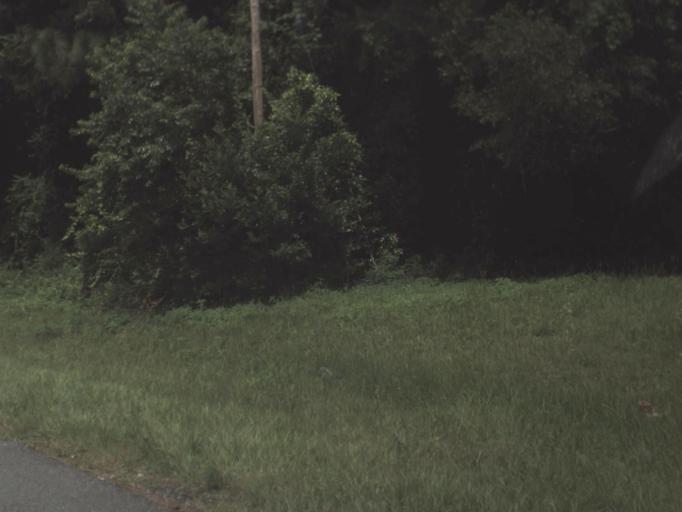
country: US
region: Florida
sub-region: Citrus County
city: Hernando
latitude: 28.9629
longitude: -82.3758
